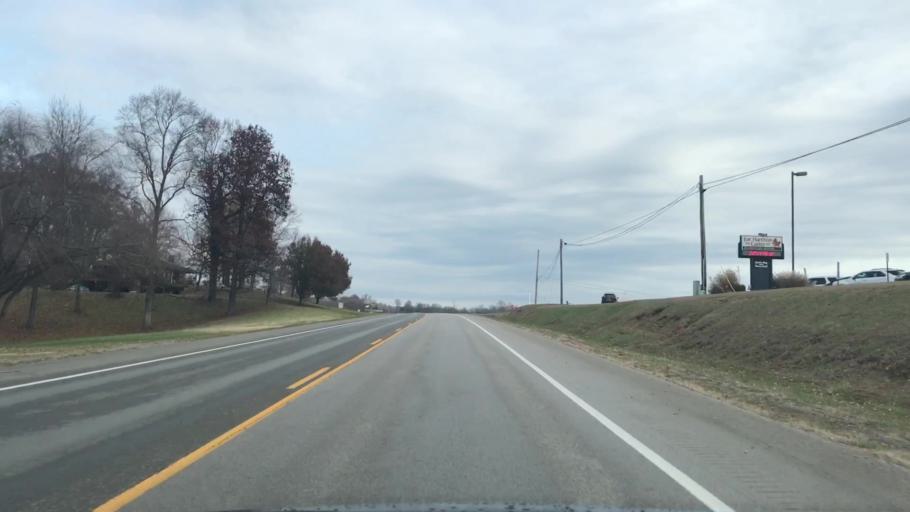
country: US
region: Kentucky
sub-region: Monroe County
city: Tompkinsville
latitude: 36.7553
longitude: -85.6895
